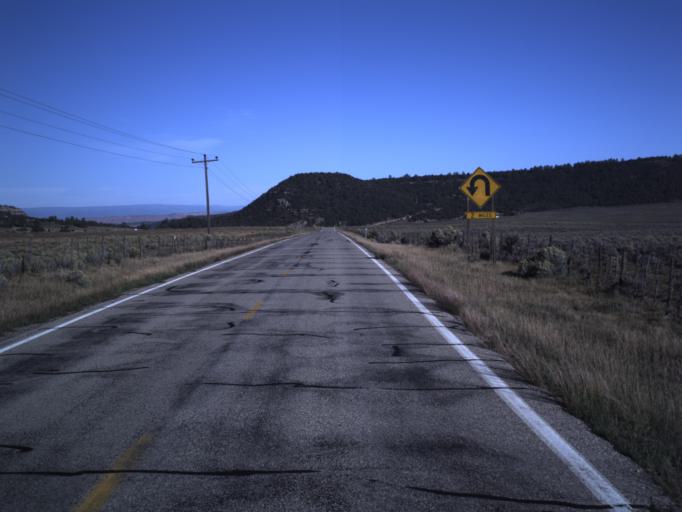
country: US
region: Utah
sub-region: Grand County
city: Moab
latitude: 38.3293
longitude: -109.1410
